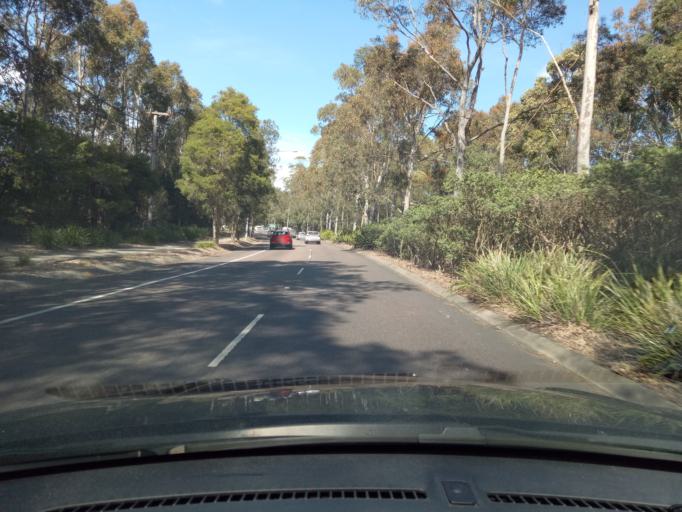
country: AU
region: New South Wales
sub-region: Wyong Shire
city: Chittaway Bay
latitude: -33.3388
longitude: 151.4292
